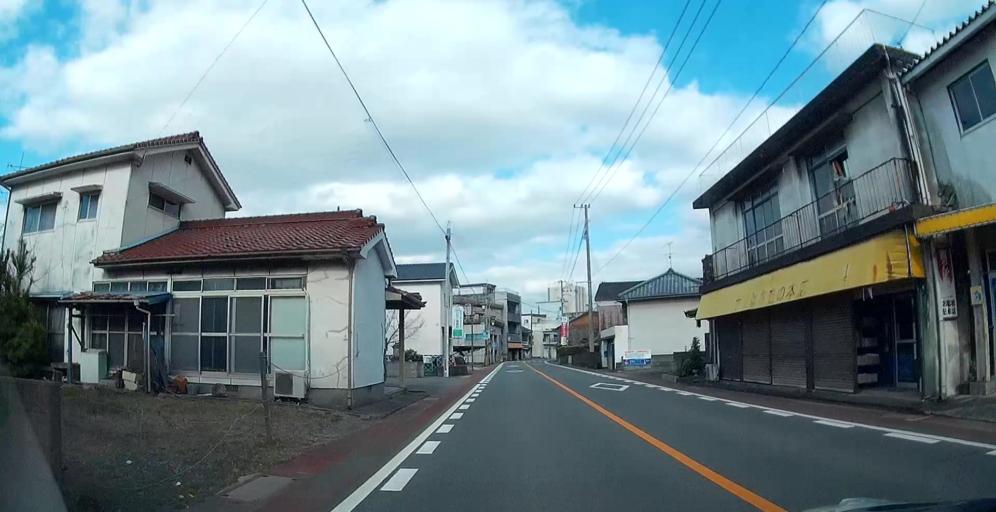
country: JP
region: Kumamoto
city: Yatsushiro
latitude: 32.4318
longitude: 130.5716
